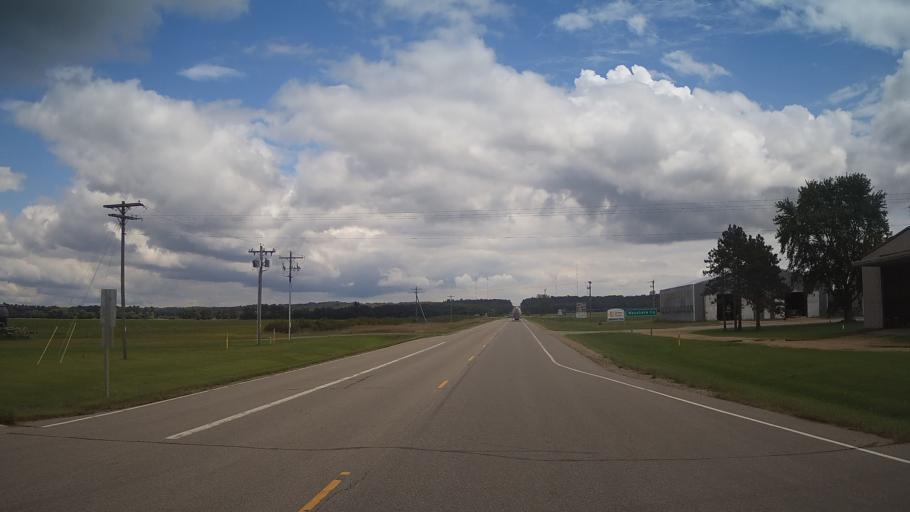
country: US
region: Wisconsin
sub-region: Marquette County
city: Westfield
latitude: 44.0222
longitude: -89.5979
